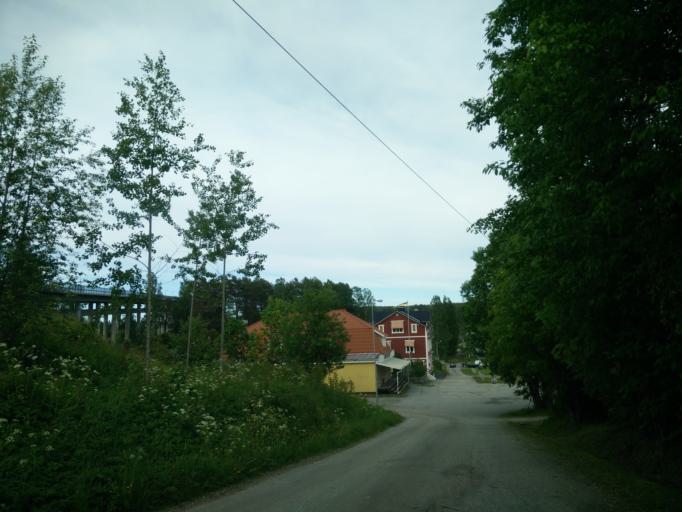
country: SE
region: Vaesternorrland
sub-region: Kramfors Kommun
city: Kramfors
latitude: 62.8812
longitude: 17.8710
